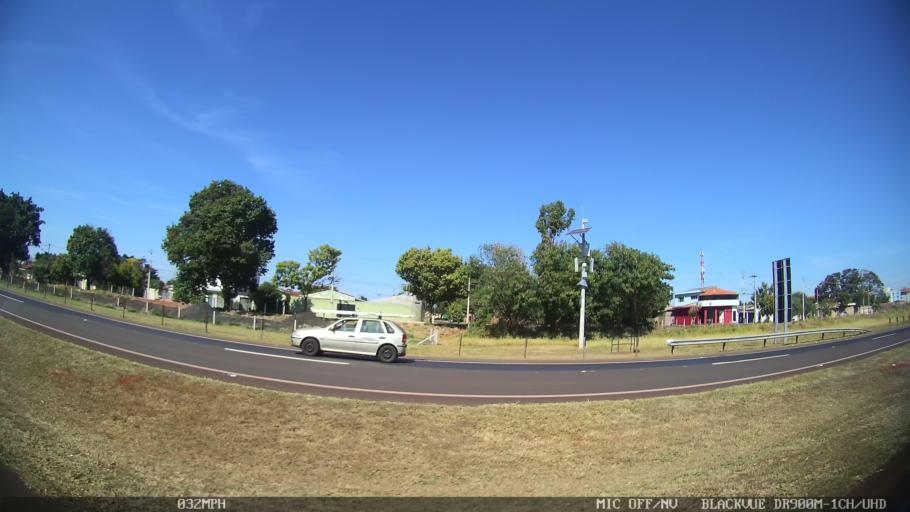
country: BR
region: Sao Paulo
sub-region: Ribeirao Preto
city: Ribeirao Preto
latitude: -21.1309
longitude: -47.8516
